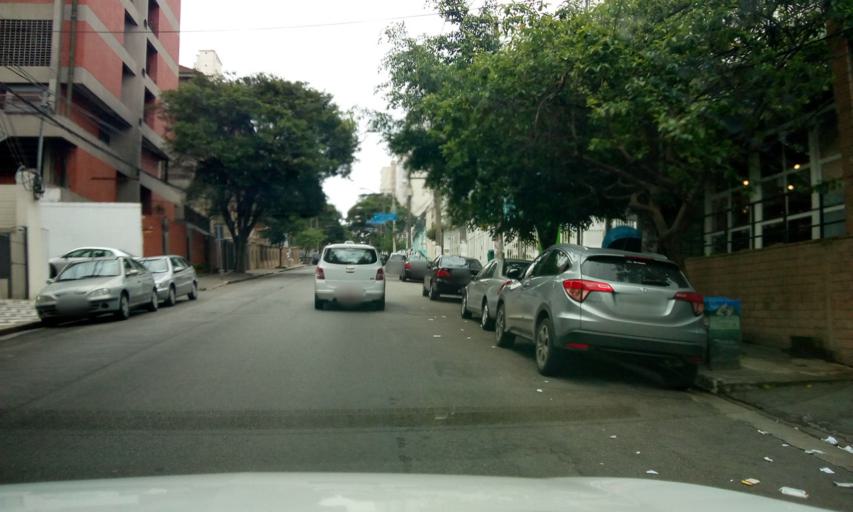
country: BR
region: Sao Paulo
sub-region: Sao Paulo
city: Sao Paulo
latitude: -23.5351
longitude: -46.6662
